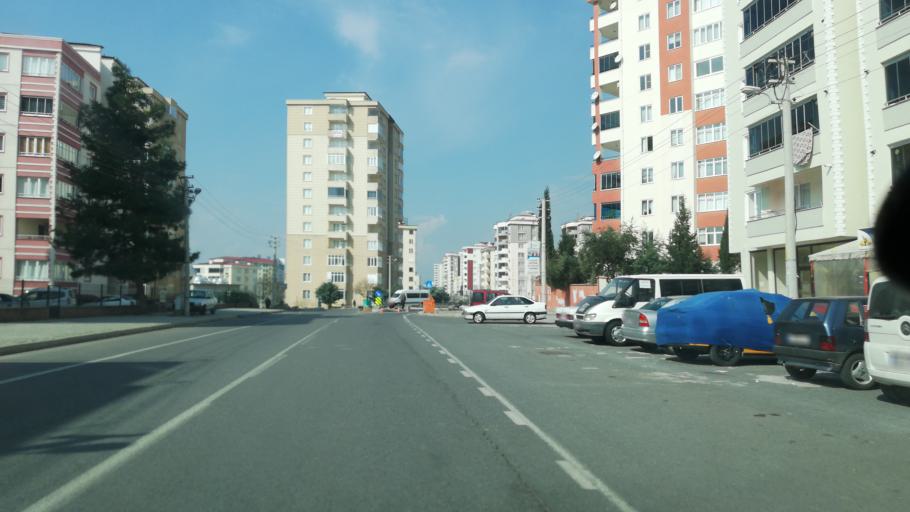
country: TR
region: Kahramanmaras
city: Kahramanmaras
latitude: 37.5873
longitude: 36.8670
